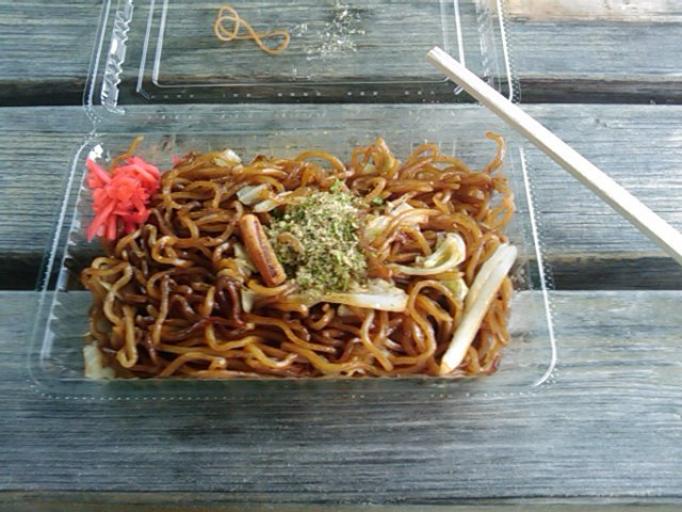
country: JP
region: Shizuoka
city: Fujinomiya
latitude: 35.1582
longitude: 138.6196
